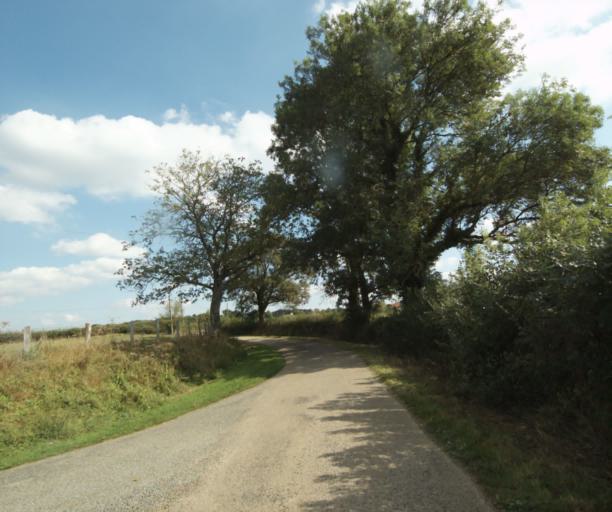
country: FR
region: Bourgogne
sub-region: Departement de Saone-et-Loire
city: Charolles
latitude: 46.4587
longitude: 4.2379
